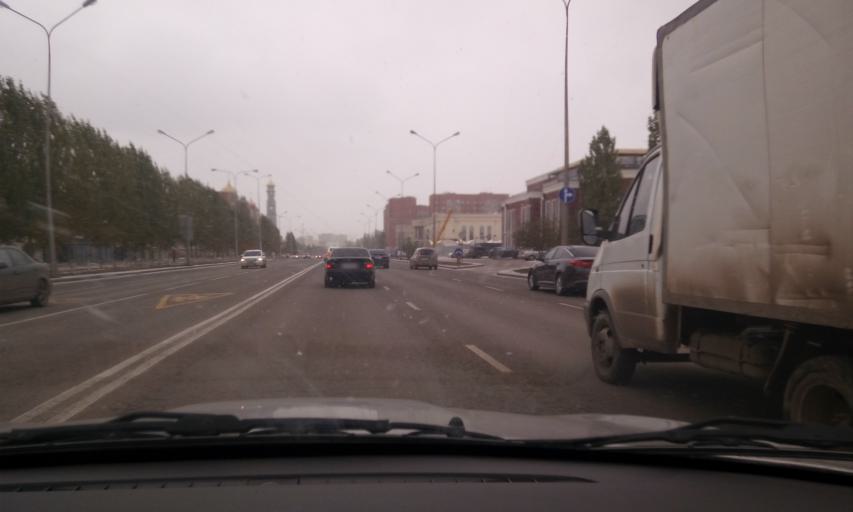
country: KZ
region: Astana Qalasy
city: Astana
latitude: 51.1451
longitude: 71.4858
